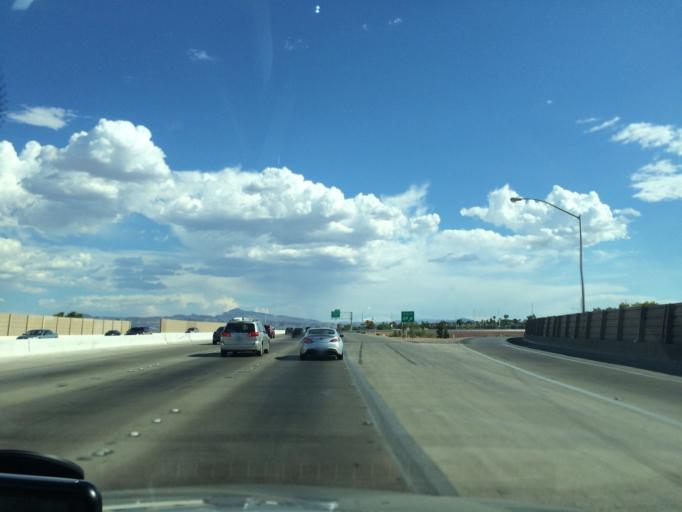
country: US
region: Nevada
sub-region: Clark County
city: Winchester
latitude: 36.1192
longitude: -115.0831
